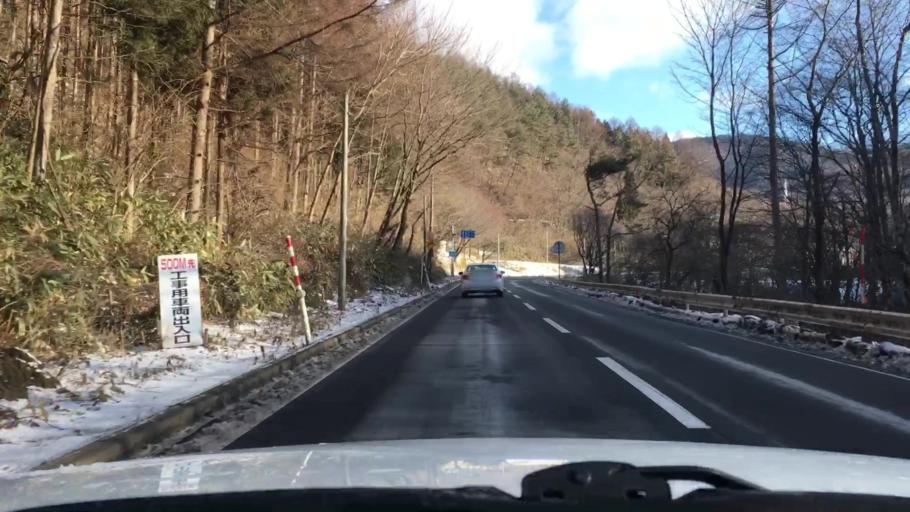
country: JP
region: Iwate
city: Morioka-shi
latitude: 39.6676
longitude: 141.3225
